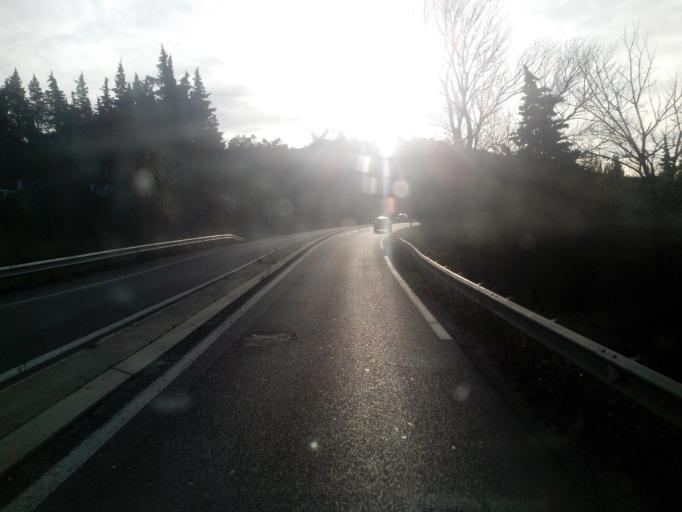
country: FR
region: Languedoc-Roussillon
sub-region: Departement de l'Aude
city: Palaja
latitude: 43.2057
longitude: 2.3888
